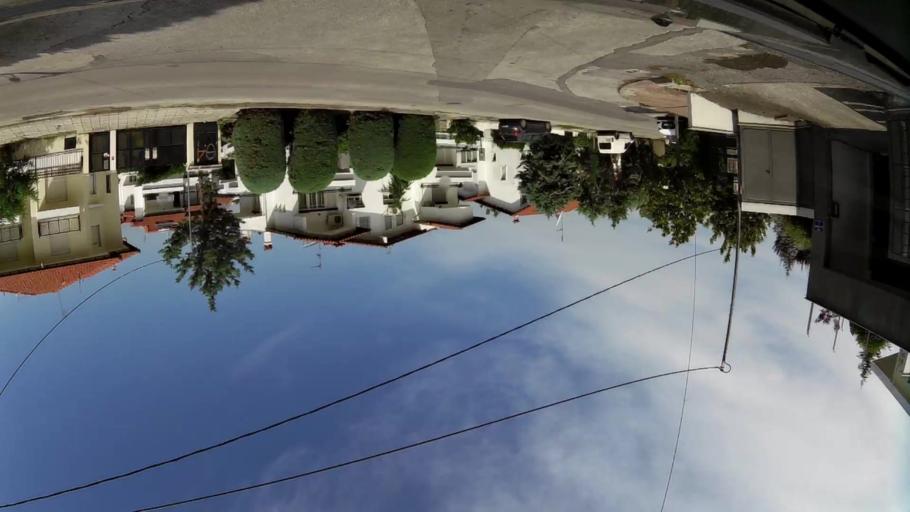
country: GR
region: Central Macedonia
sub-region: Nomos Thessalonikis
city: Panorama
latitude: 40.5818
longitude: 23.0210
